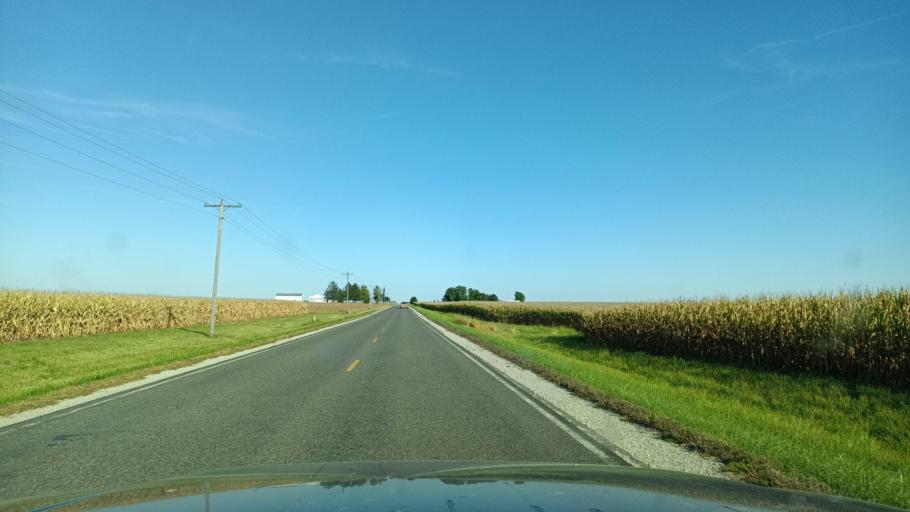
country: US
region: Illinois
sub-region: De Witt County
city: Clinton
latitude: 40.2244
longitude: -88.8820
